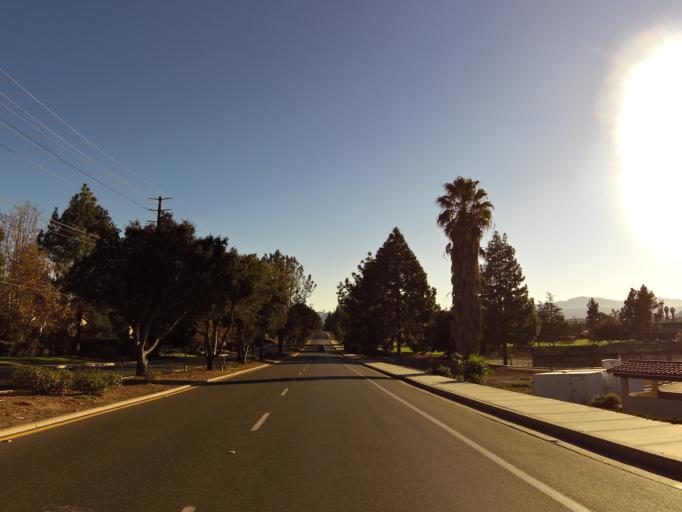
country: US
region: California
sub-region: Ventura County
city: Thousand Oaks
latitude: 34.2156
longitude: -118.8684
